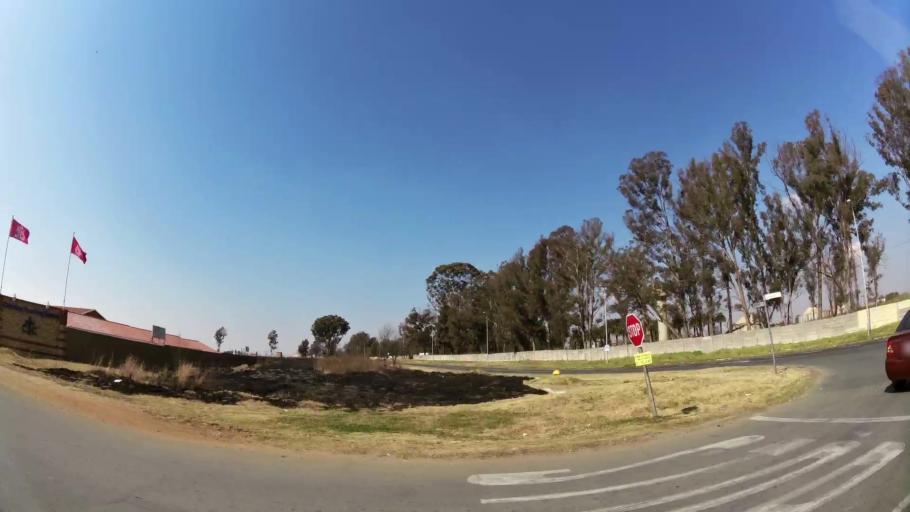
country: ZA
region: Gauteng
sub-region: Ekurhuleni Metropolitan Municipality
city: Benoni
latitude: -26.2075
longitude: 28.3147
